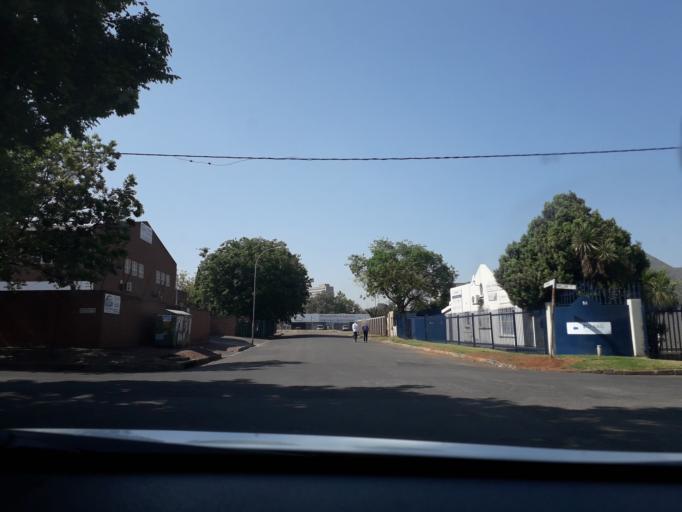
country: ZA
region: Gauteng
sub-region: City of Johannesburg Metropolitan Municipality
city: Modderfontein
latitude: -26.1100
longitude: 28.2343
